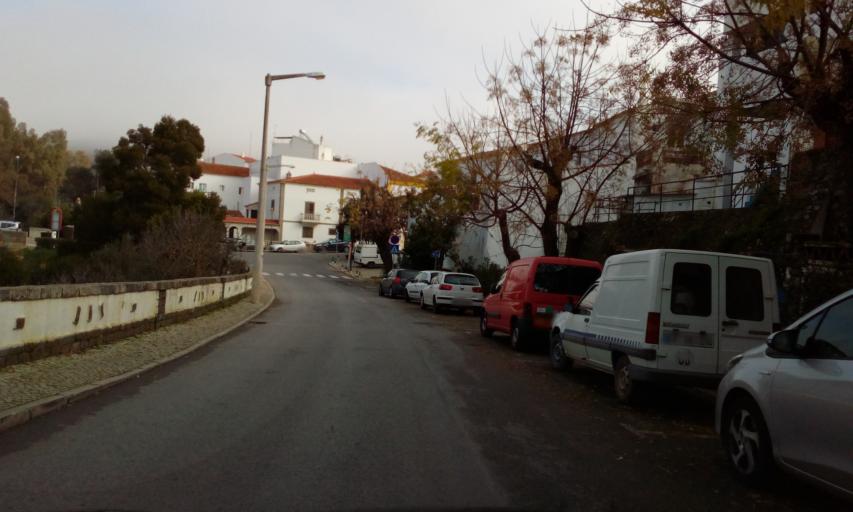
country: PT
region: Faro
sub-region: Alcoutim
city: Alcoutim
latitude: 37.4711
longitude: -7.4731
